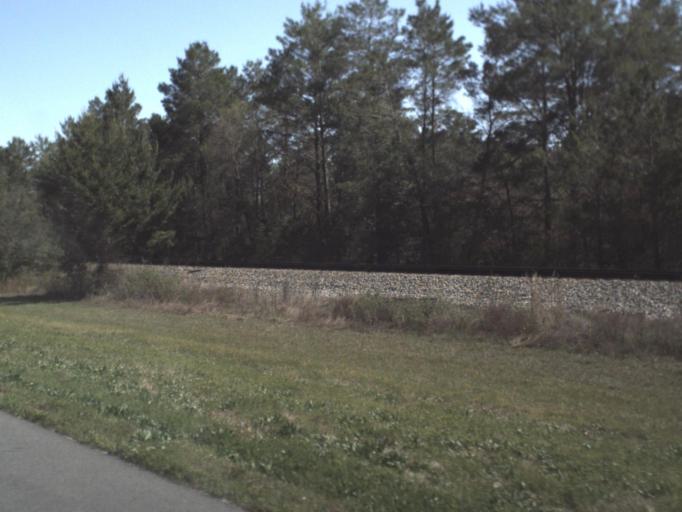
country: US
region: Florida
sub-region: Okaloosa County
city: Crestview
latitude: 30.7394
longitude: -86.3681
